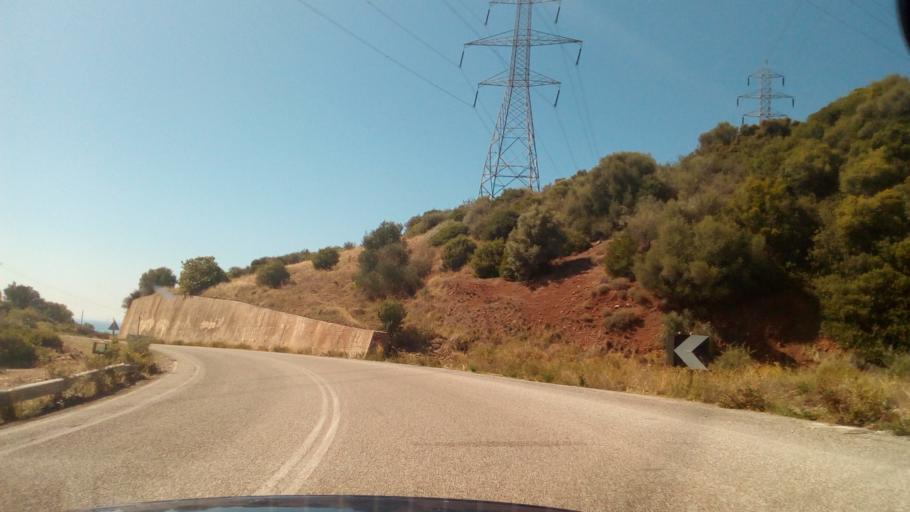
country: GR
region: West Greece
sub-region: Nomos Achaias
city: Kamarai
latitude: 38.4058
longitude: 21.9824
